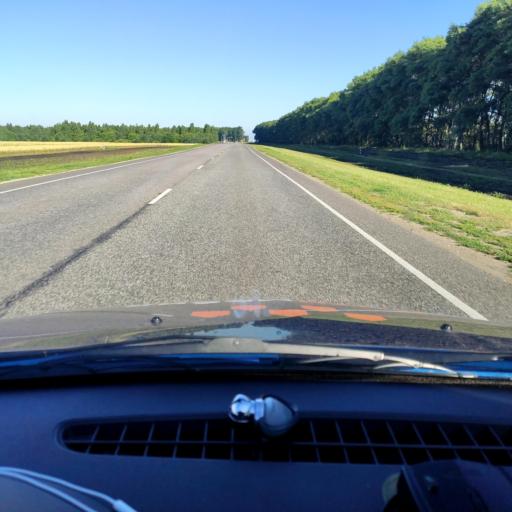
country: RU
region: Orjol
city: Pokrovskoye
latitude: 52.6383
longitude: 36.6802
